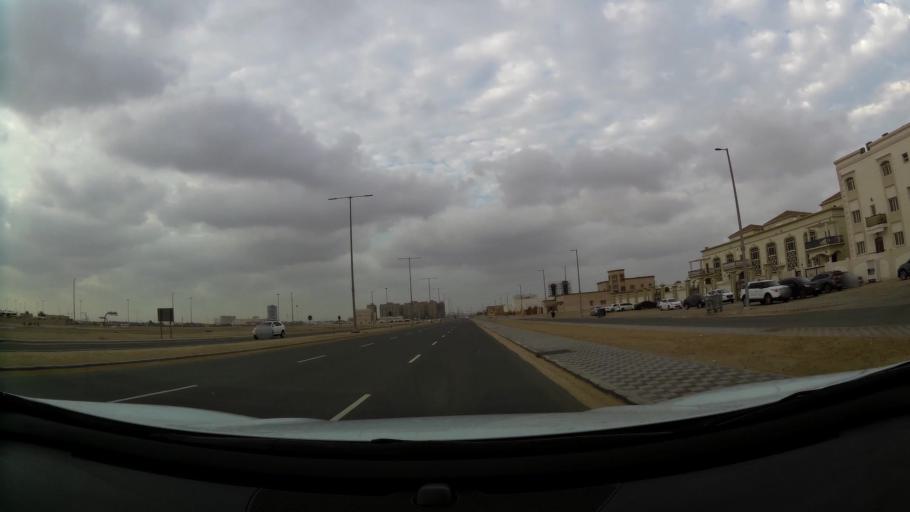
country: AE
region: Abu Dhabi
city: Abu Dhabi
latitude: 24.3595
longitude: 54.5401
